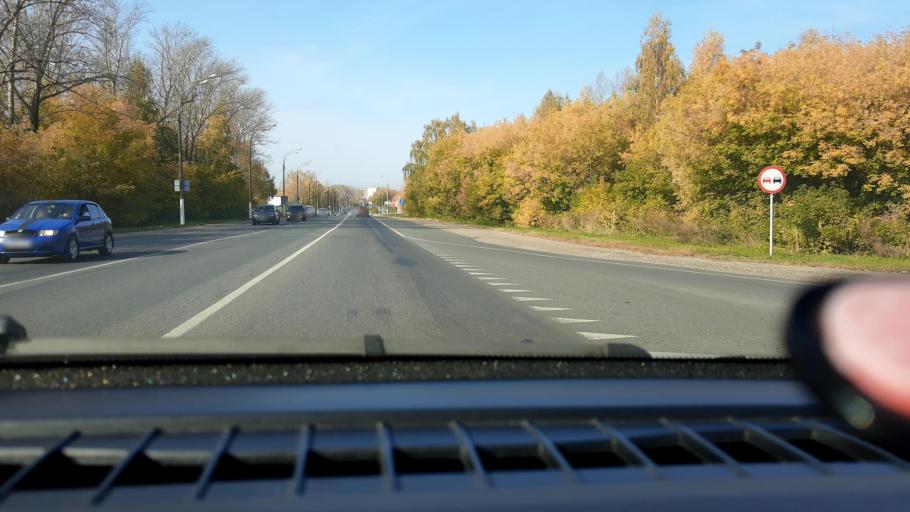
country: RU
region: Nizjnij Novgorod
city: Kstovo
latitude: 56.1415
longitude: 44.2270
